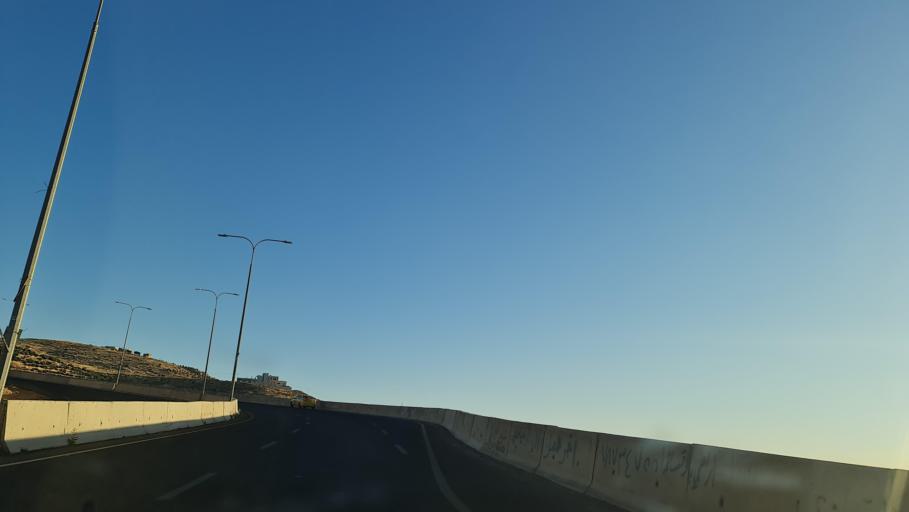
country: JO
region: Zarqa
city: Russeifa
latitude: 32.0927
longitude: 35.9610
